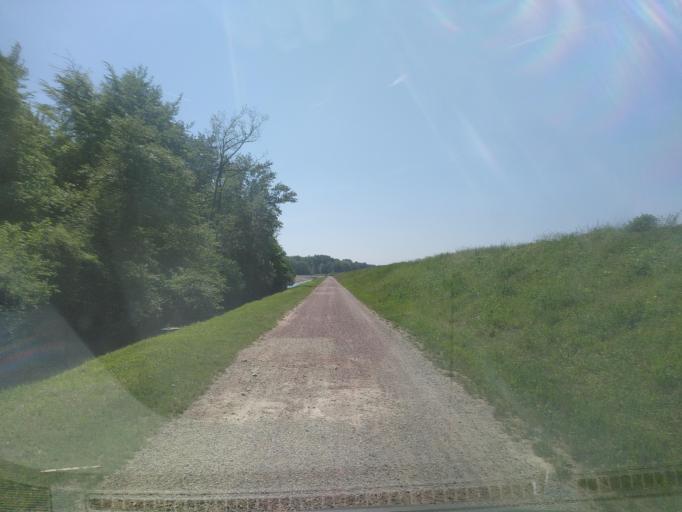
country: DE
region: Baden-Wuerttemberg
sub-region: Freiburg Region
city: Breisach am Rhein
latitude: 48.0623
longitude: 7.5745
